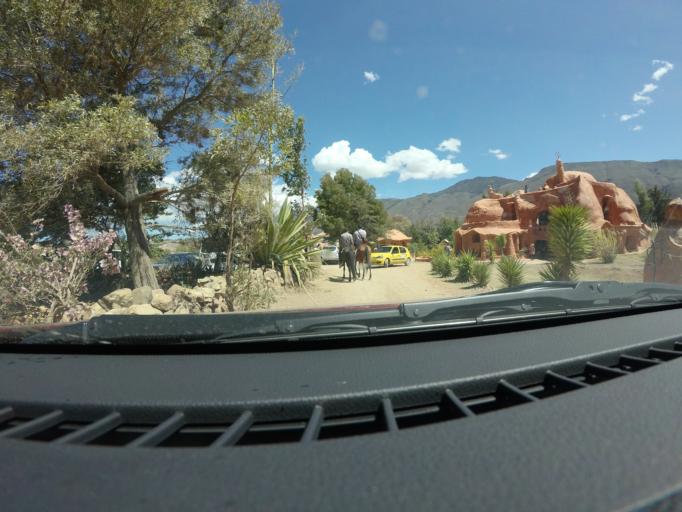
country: CO
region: Boyaca
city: Villa de Leiva
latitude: 5.6349
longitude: -73.5369
